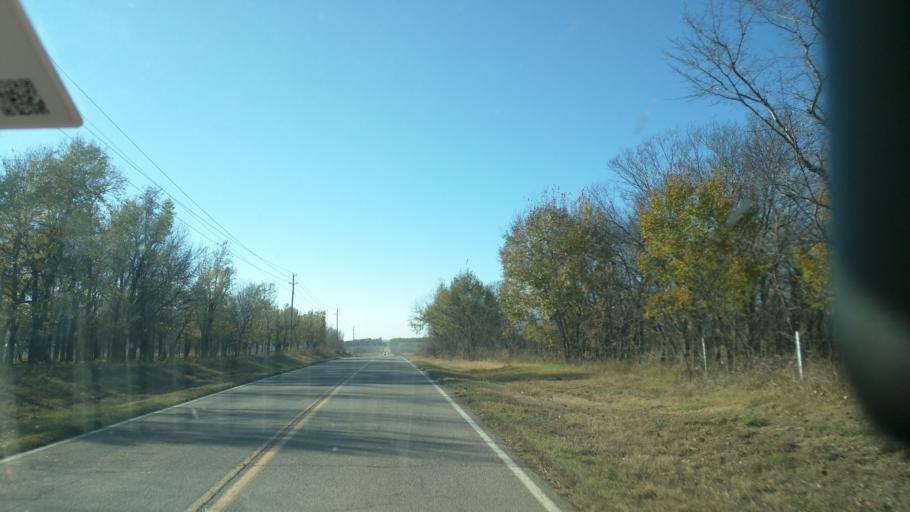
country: US
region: Oklahoma
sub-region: Nowata County
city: Nowata
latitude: 36.7717
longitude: -95.5536
